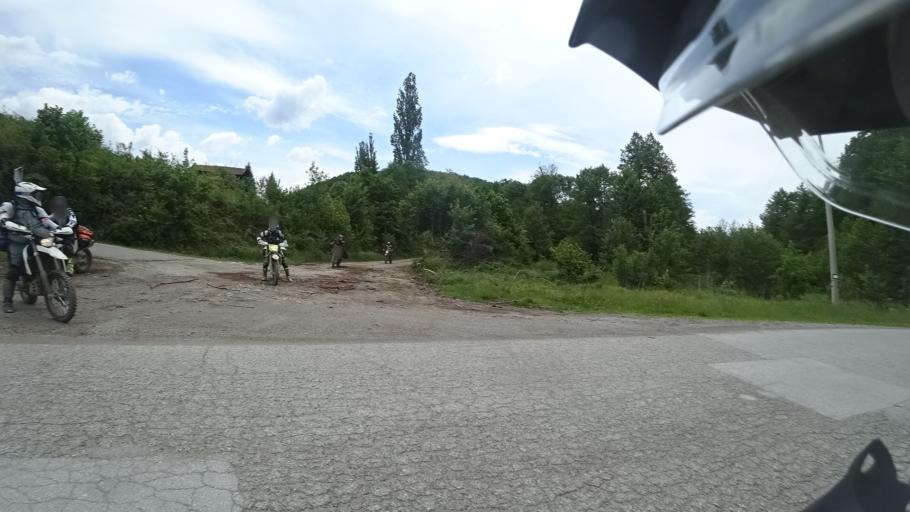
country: HR
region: Karlovacka
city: Vojnic
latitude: 45.2482
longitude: 15.6665
